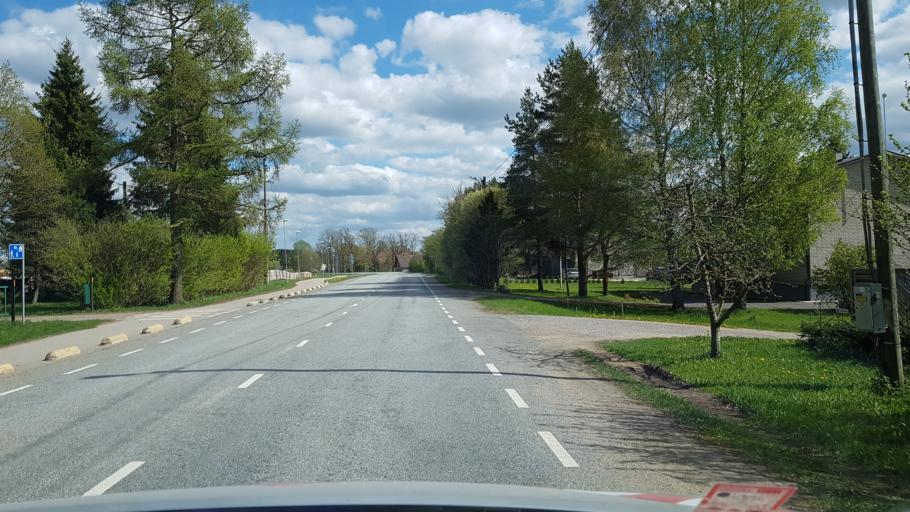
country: EE
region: Tartu
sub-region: UElenurme vald
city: Ulenurme
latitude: 58.2983
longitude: 26.8714
